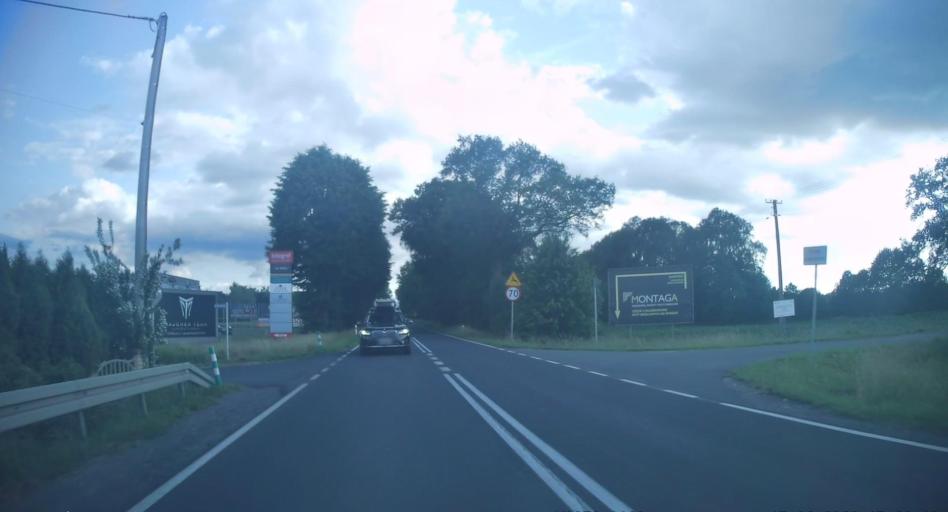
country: PL
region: Lesser Poland Voivodeship
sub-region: Powiat oswiecimski
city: Grojec
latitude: 49.9584
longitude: 19.2141
